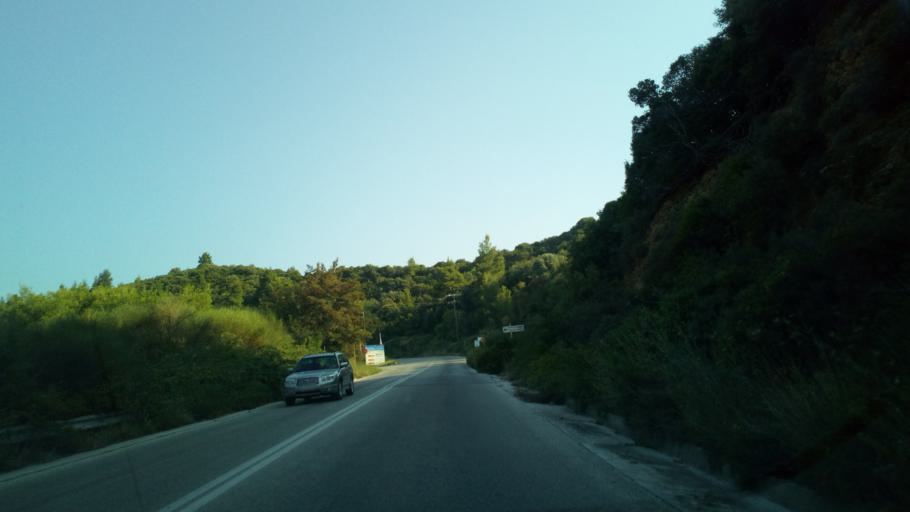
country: GR
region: Central Macedonia
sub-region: Nomos Chalkidikis
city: Neos Marmaras
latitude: 40.1702
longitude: 23.8601
